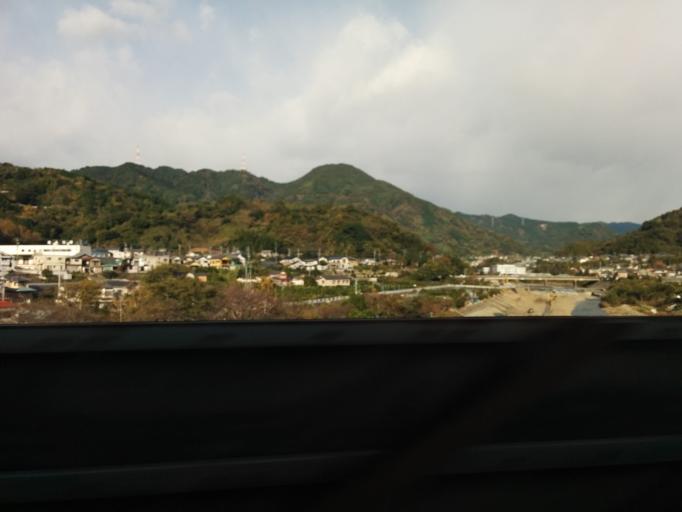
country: JP
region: Shizuoka
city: Fujinomiya
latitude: 35.0749
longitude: 138.5241
